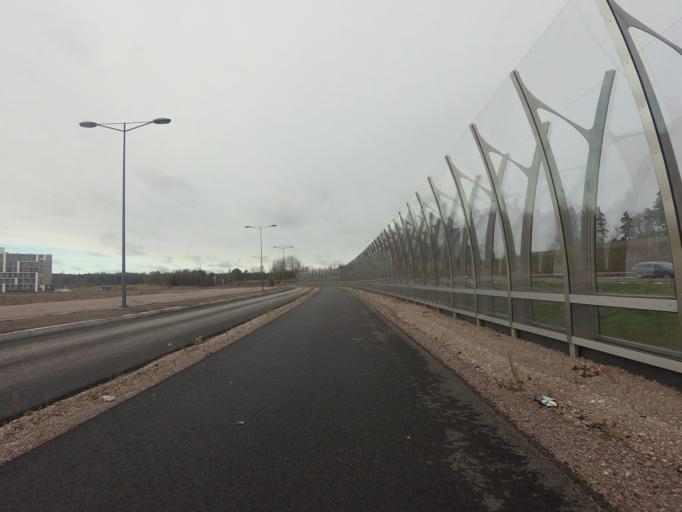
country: FI
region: Uusimaa
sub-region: Helsinki
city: Kauniainen
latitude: 60.1902
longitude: 24.7457
